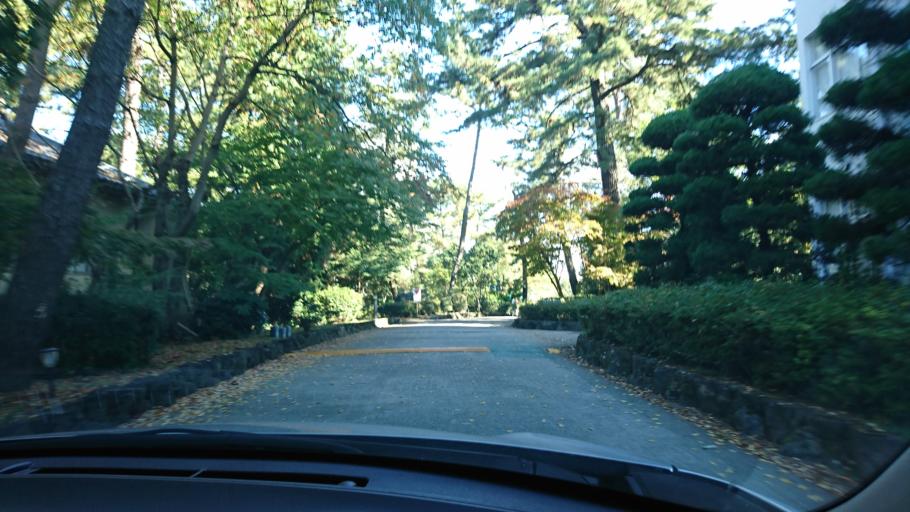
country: JP
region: Hyogo
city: Kakogawacho-honmachi
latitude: 34.7467
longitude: 134.8826
